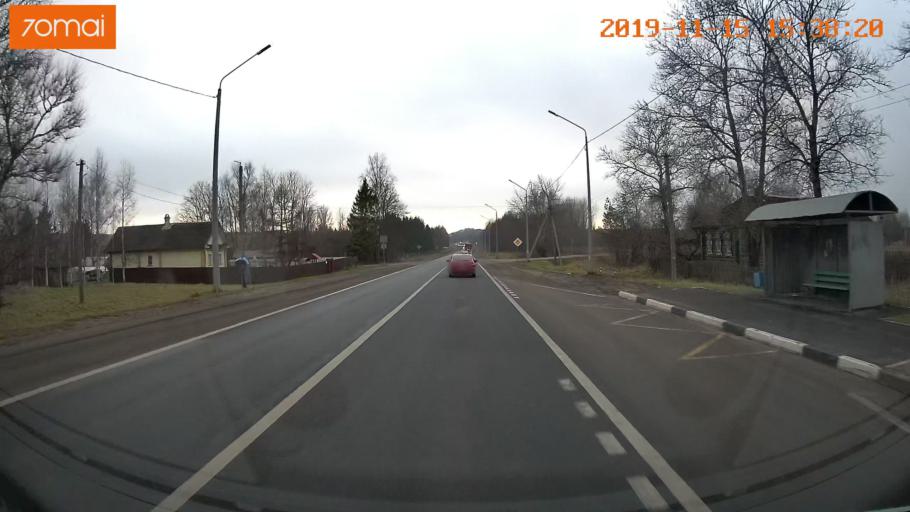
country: RU
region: Jaroslavl
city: Danilov
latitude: 58.0307
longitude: 40.0815
